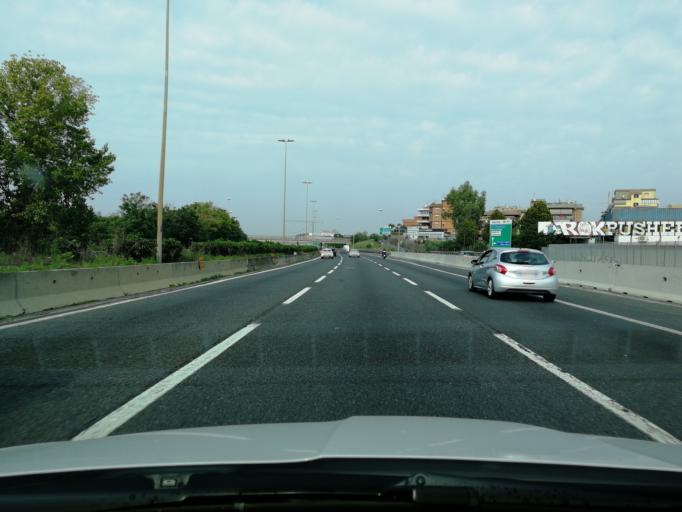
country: IT
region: Latium
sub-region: Citta metropolitana di Roma Capitale
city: Setteville
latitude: 41.8869
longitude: 12.6137
